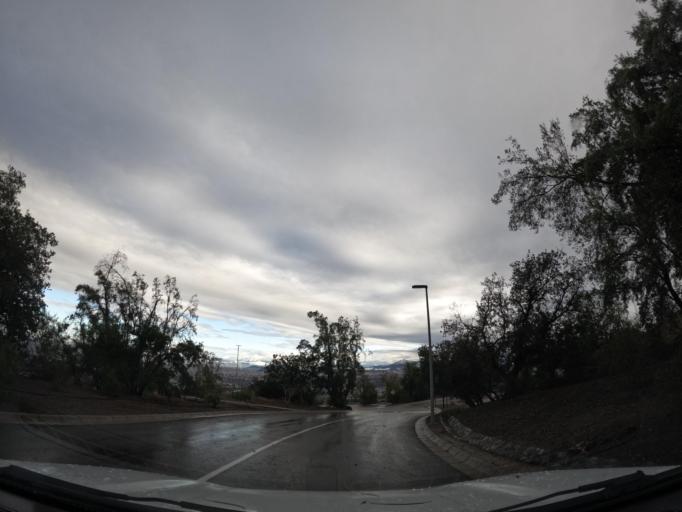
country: CL
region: Santiago Metropolitan
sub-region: Provincia de Santiago
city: Villa Presidente Frei, Nunoa, Santiago, Chile
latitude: -33.4764
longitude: -70.5133
